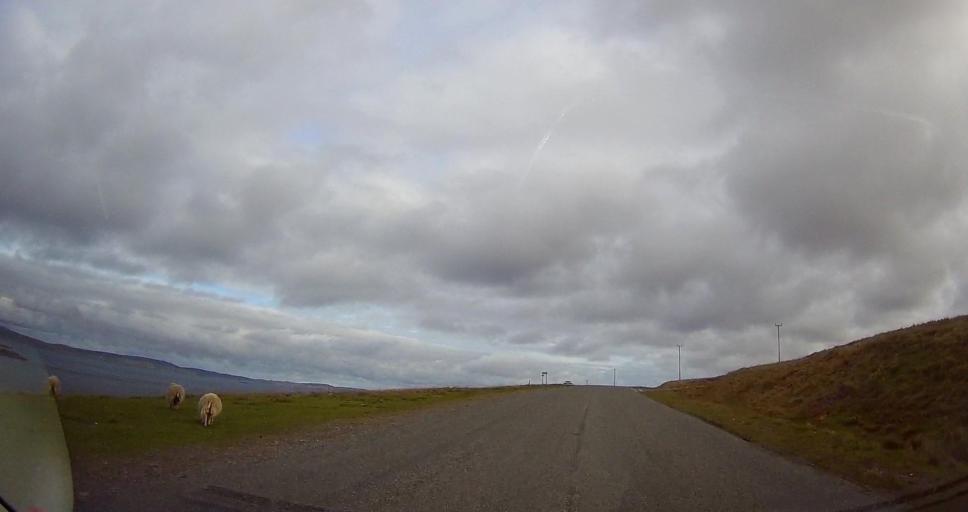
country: GB
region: Scotland
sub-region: Shetland Islands
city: Shetland
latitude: 60.5078
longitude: -1.1658
